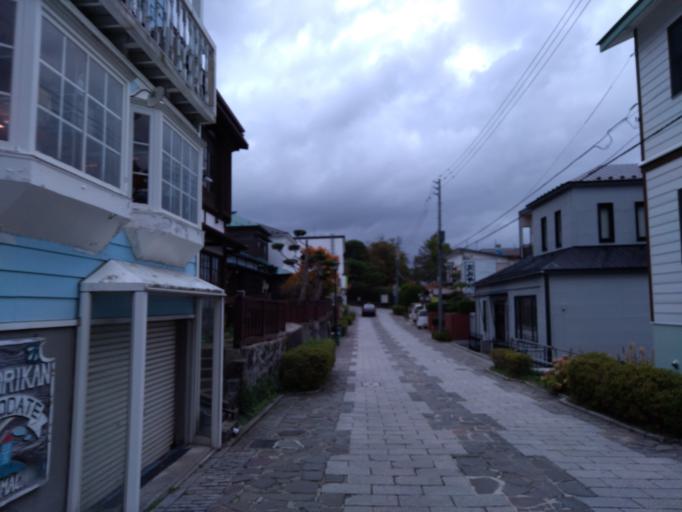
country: JP
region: Hokkaido
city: Hakodate
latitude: 41.7643
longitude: 140.7107
